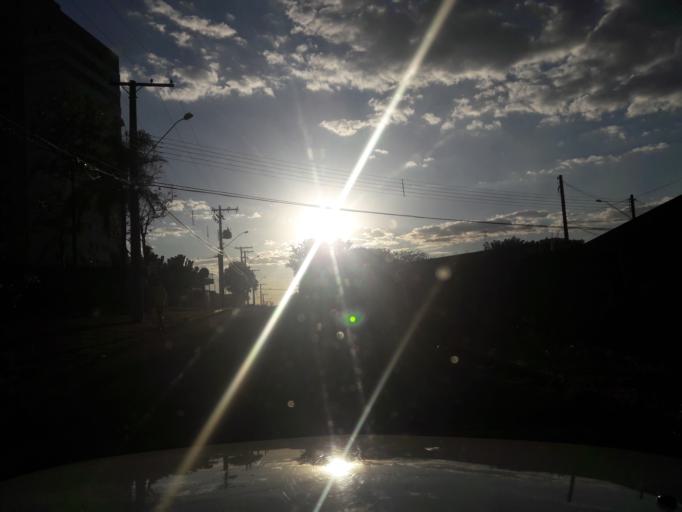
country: BR
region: Sao Paulo
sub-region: Moji-Guacu
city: Mogi-Gaucu
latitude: -22.3957
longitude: -46.9482
